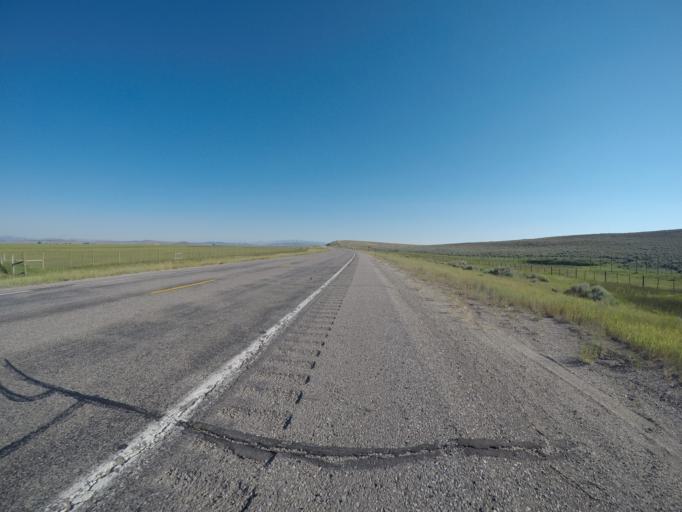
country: US
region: Wyoming
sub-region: Sublette County
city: Pinedale
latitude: 42.9348
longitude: -110.0813
